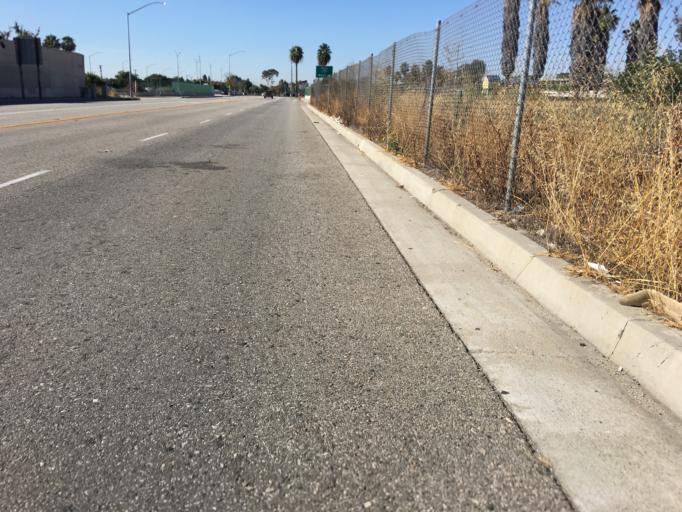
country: US
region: California
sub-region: Los Angeles County
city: Norwalk
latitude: 33.9154
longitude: -118.1035
